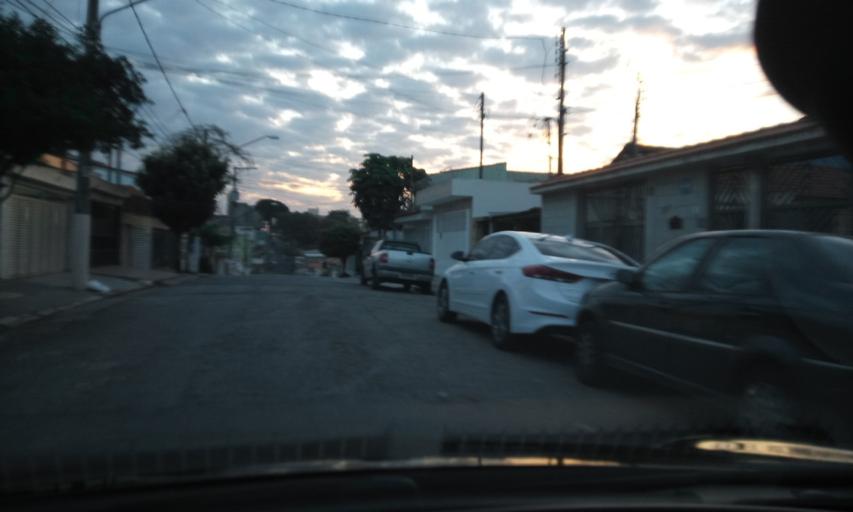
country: BR
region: Sao Paulo
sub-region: Sao Bernardo Do Campo
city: Sao Bernardo do Campo
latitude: -23.6958
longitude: -46.5645
